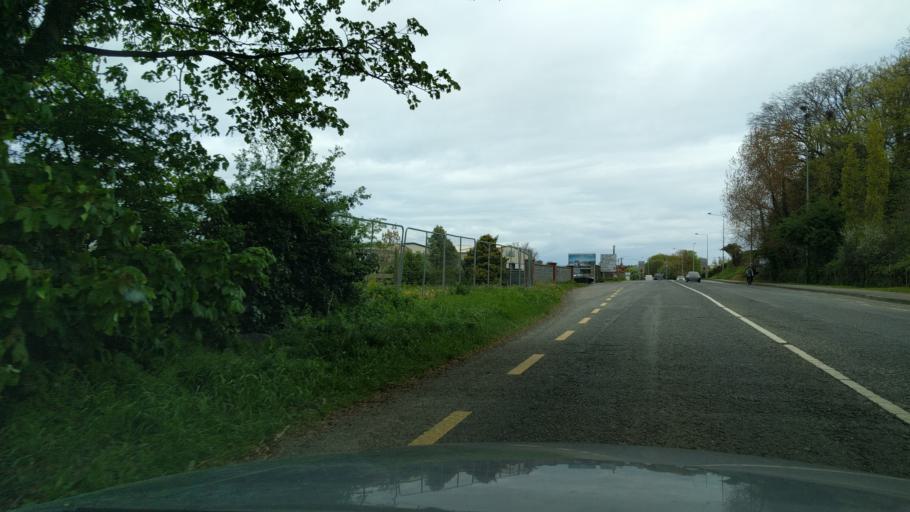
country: IE
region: Leinster
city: Balrothery
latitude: 53.5857
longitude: -6.1920
